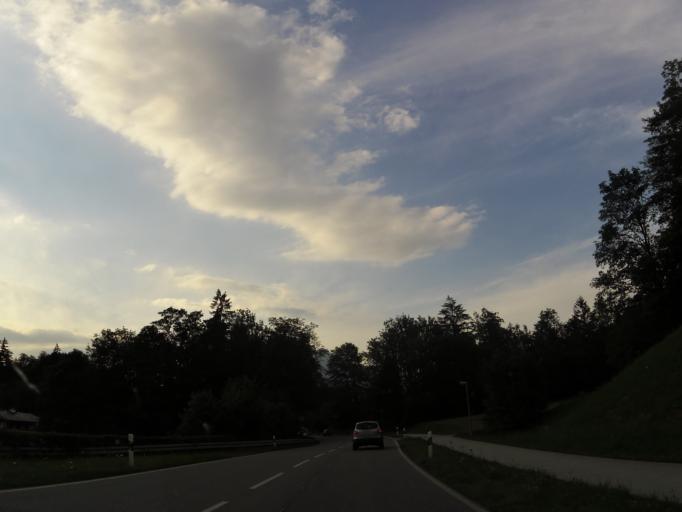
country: DE
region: Bavaria
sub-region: Upper Bavaria
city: Berchtesgaden
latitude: 47.6162
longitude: 13.0003
